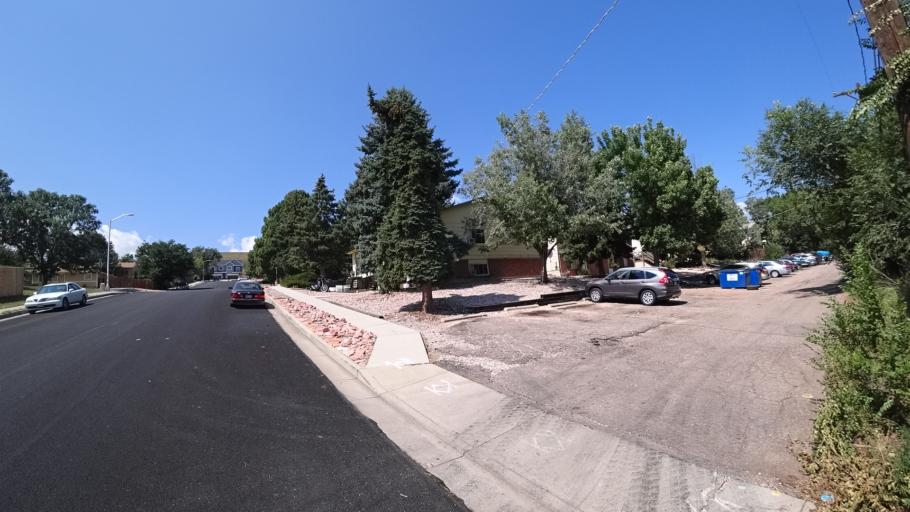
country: US
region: Colorado
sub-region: El Paso County
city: Colorado Springs
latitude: 38.8737
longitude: -104.8378
